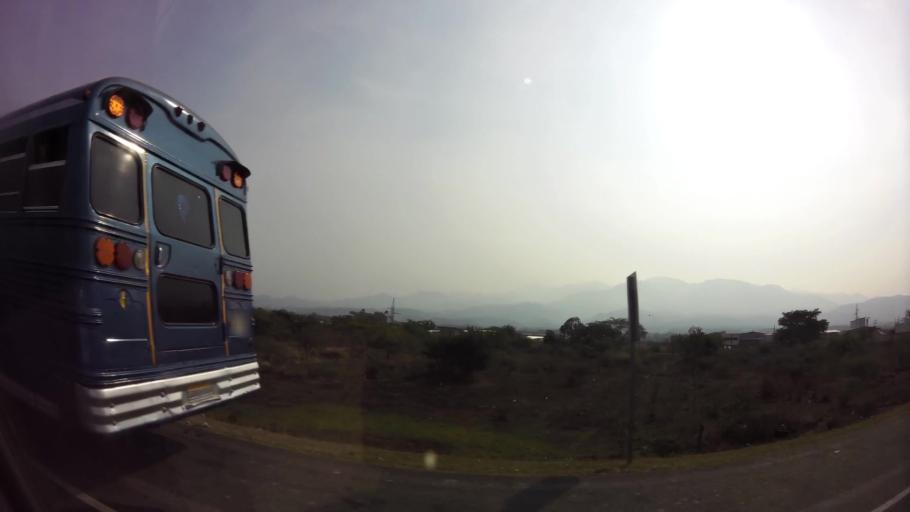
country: HN
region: Comayagua
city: Comayagua
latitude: 14.4226
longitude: -87.6295
